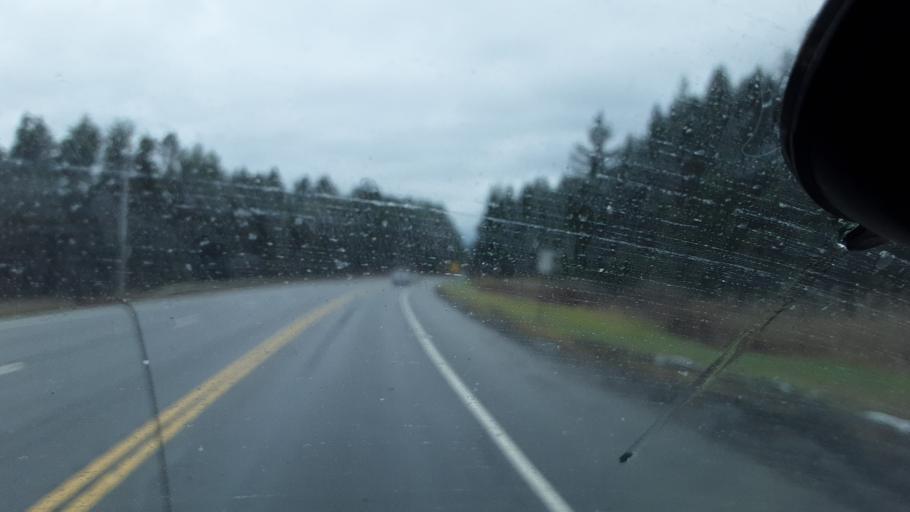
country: US
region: New York
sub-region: Cattaraugus County
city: Yorkshire
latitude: 42.5900
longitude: -78.4945
